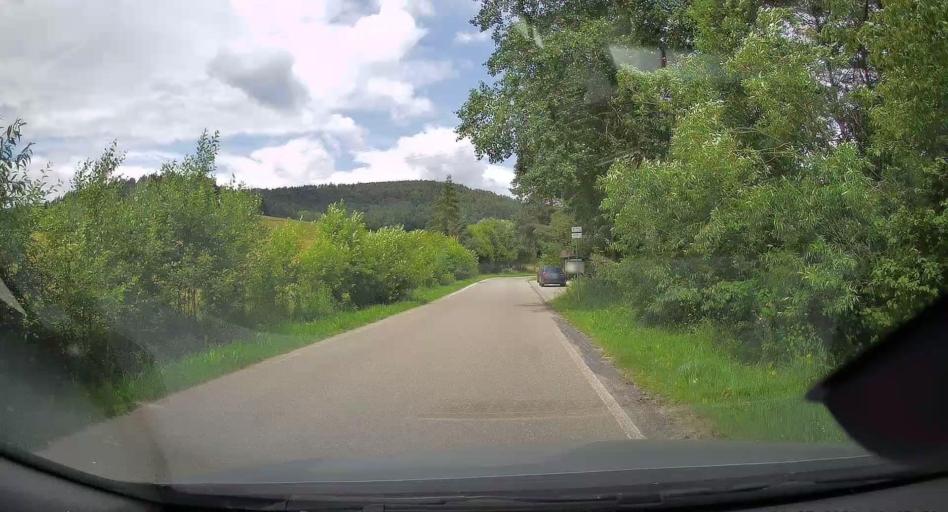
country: PL
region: Lesser Poland Voivodeship
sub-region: Powiat nowosadecki
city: Muszyna
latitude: 49.3874
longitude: 20.9026
